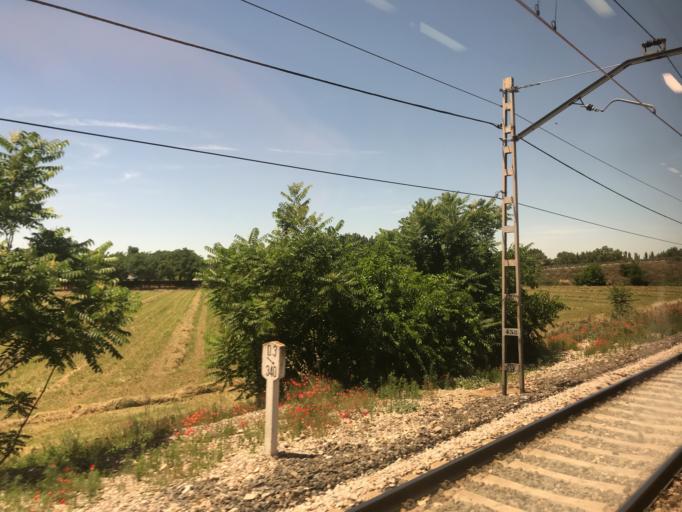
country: ES
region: Madrid
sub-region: Provincia de Madrid
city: Aranjuez
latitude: 40.0432
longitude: -3.6213
